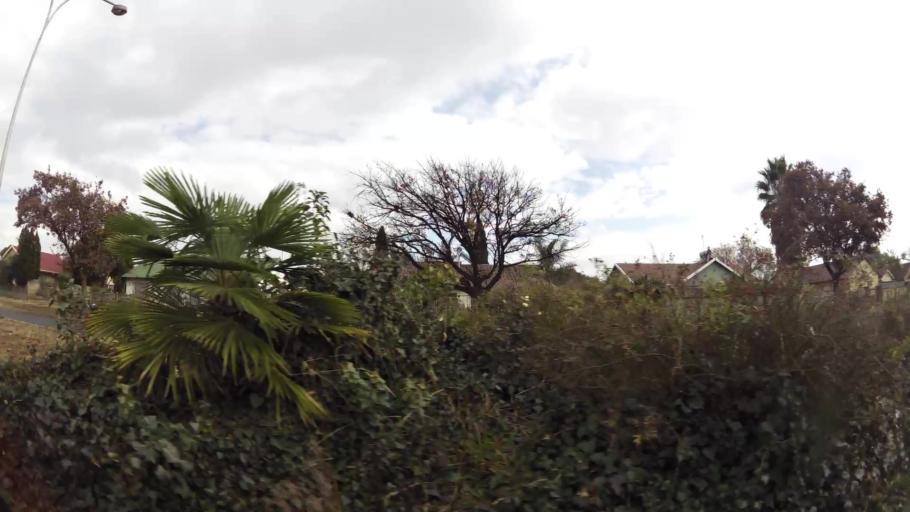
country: ZA
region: Gauteng
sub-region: Sedibeng District Municipality
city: Vanderbijlpark
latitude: -26.7214
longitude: 27.8630
